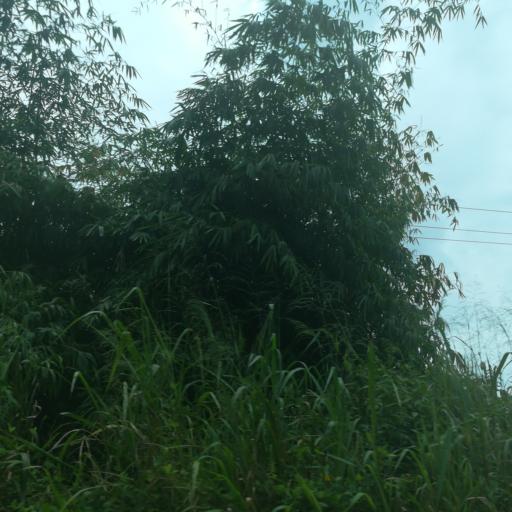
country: NG
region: Ogun
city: Odogbolu
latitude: 6.6601
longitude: 3.7113
